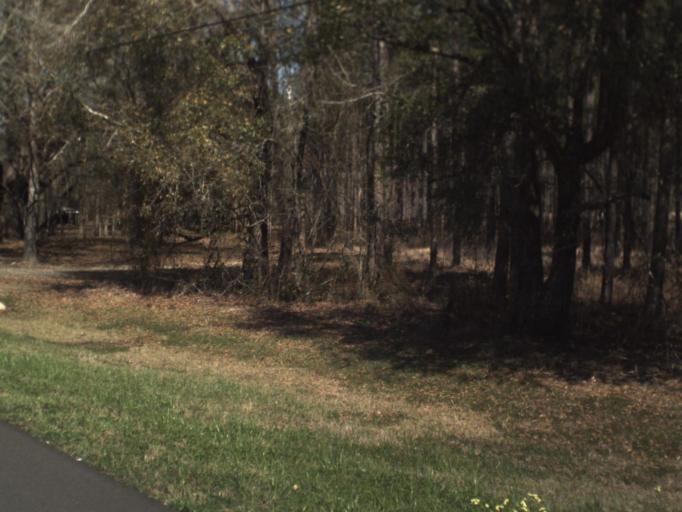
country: US
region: Florida
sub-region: Jackson County
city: Sneads
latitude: 30.7952
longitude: -85.0269
